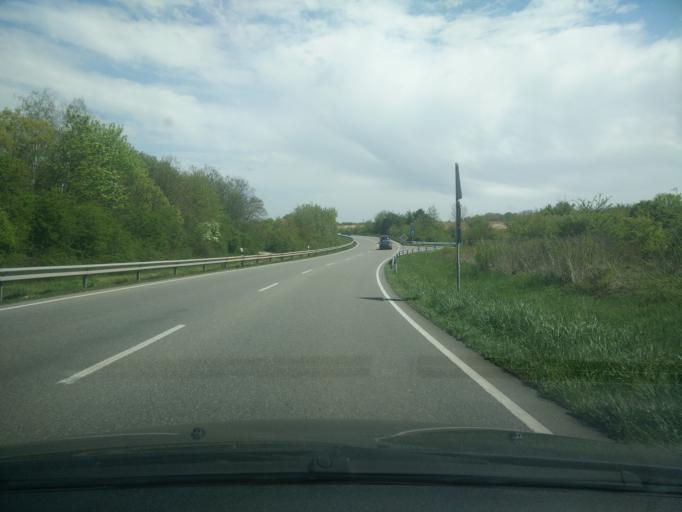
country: DE
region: Rheinland-Pfalz
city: Insheim
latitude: 49.1739
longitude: 8.1387
